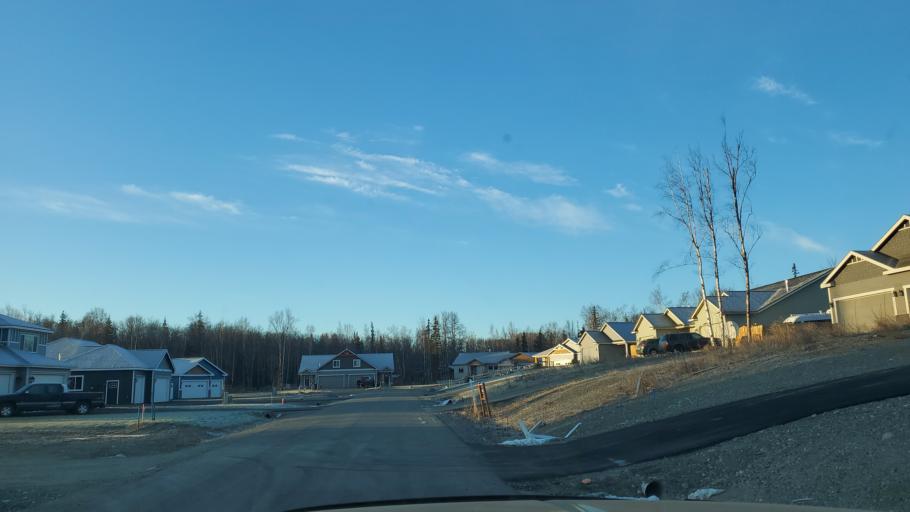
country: US
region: Alaska
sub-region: Matanuska-Susitna Borough
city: Wasilla
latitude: 61.5903
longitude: -149.4549
